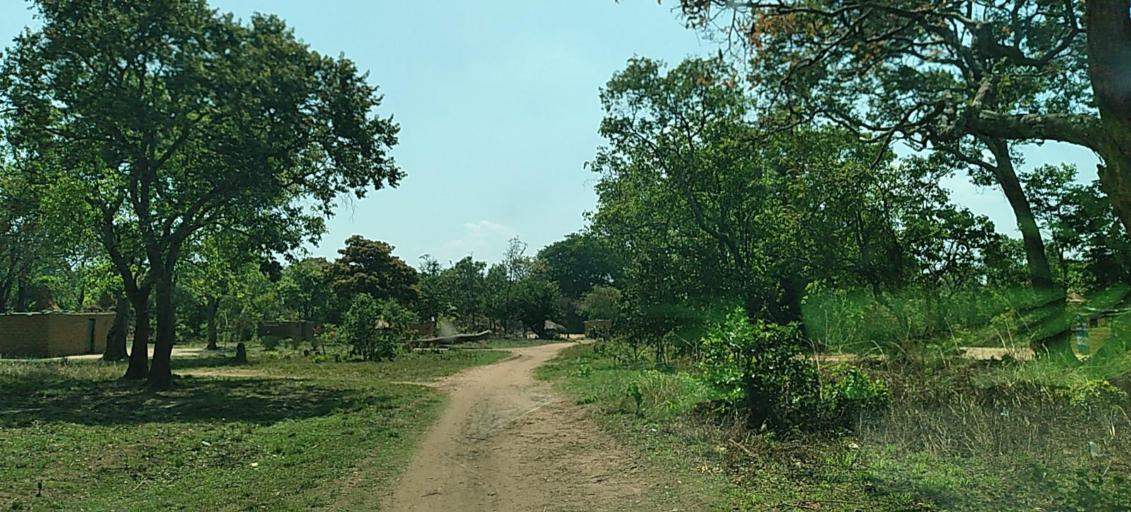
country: CD
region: Katanga
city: Kolwezi
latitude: -11.2782
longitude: 25.1204
